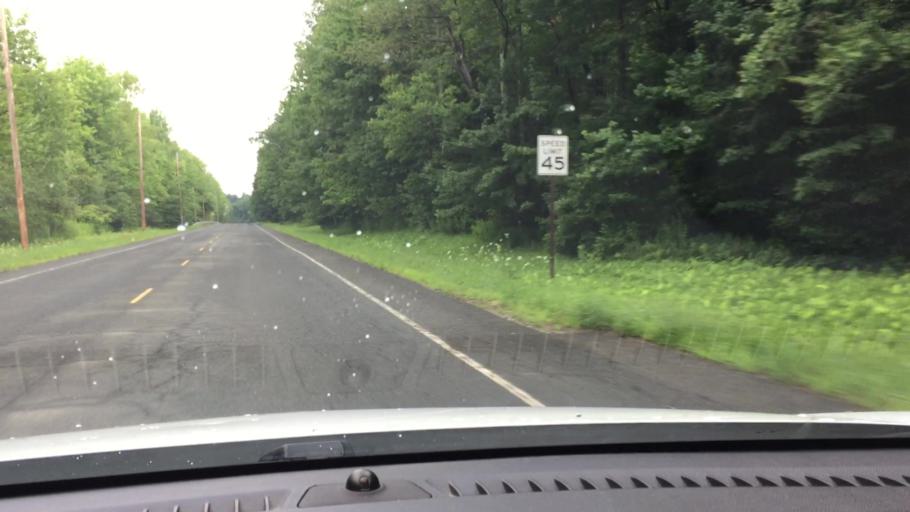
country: US
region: Massachusetts
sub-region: Berkshire County
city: Becket
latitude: 42.4252
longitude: -73.0033
